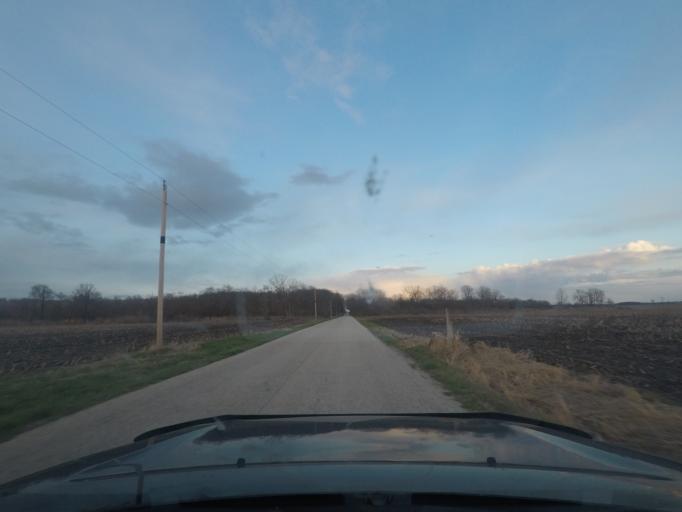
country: US
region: Indiana
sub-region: LaPorte County
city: Kingsford Heights
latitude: 41.4619
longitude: -86.7160
